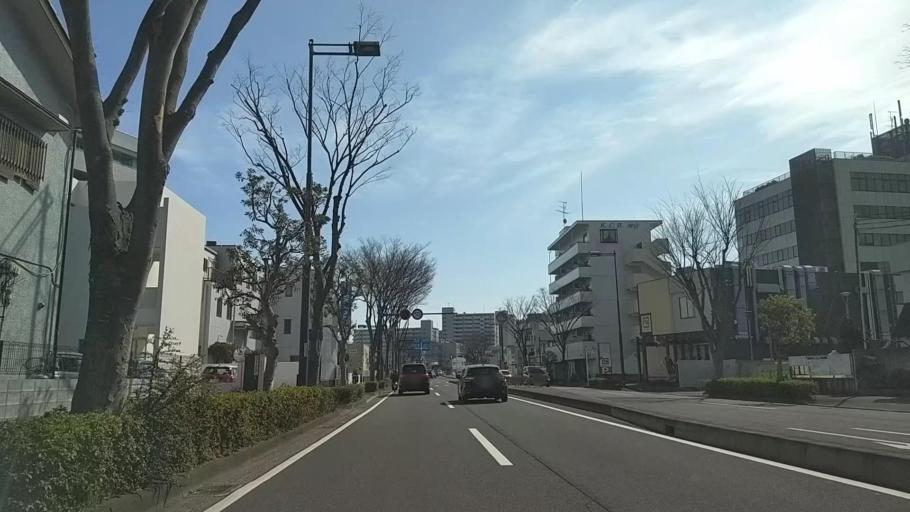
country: JP
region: Kanagawa
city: Fujisawa
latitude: 35.3434
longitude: 139.4490
